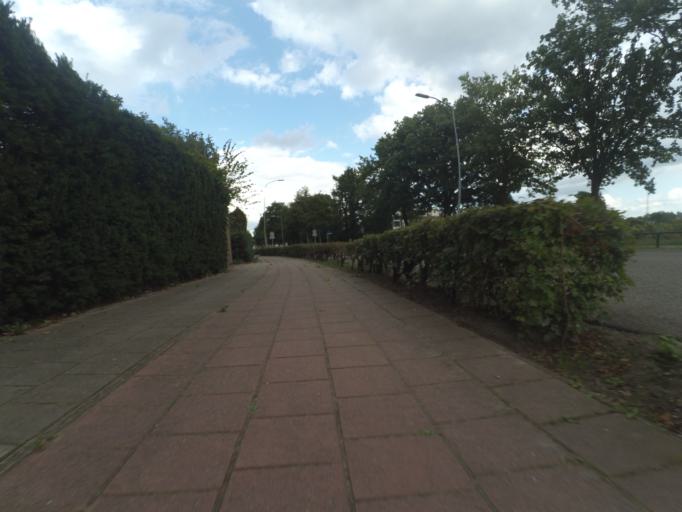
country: NL
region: Utrecht
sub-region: Gemeente Utrechtse Heuvelrug
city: Overberg
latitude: 52.0750
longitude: 5.4945
